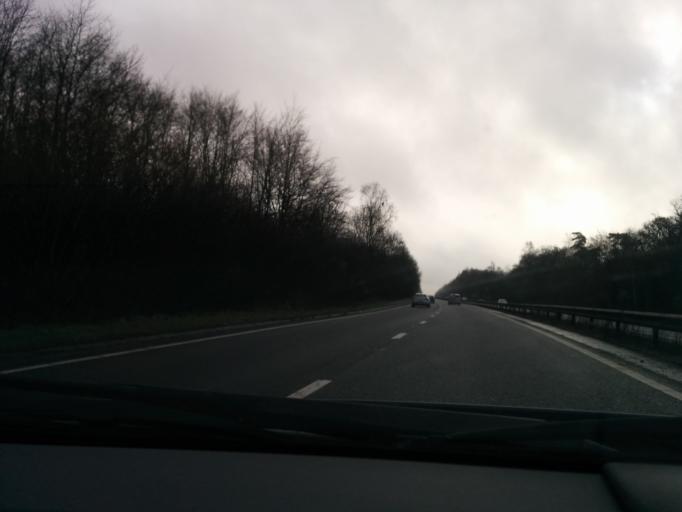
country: GB
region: England
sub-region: Hampshire
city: Highclere
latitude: 51.2731
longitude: -1.3437
